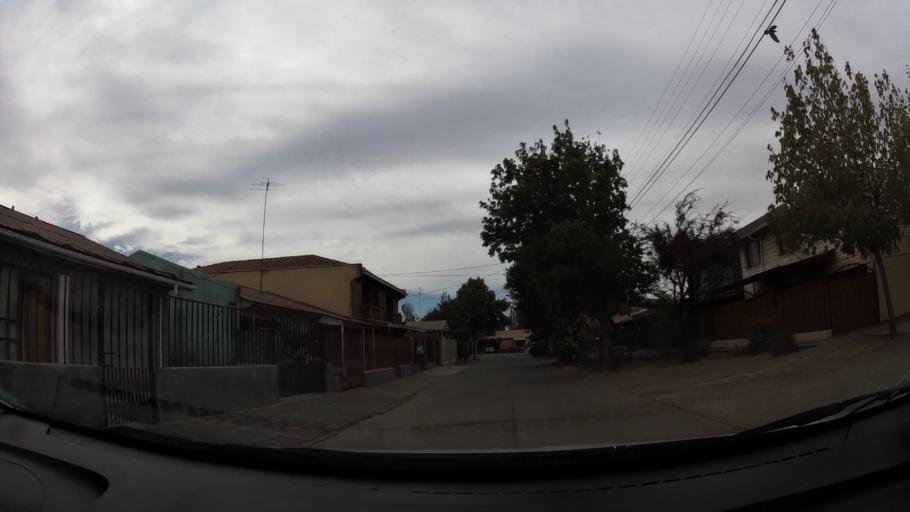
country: CL
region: O'Higgins
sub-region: Provincia de Cachapoal
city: Rancagua
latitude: -34.1537
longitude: -70.7425
